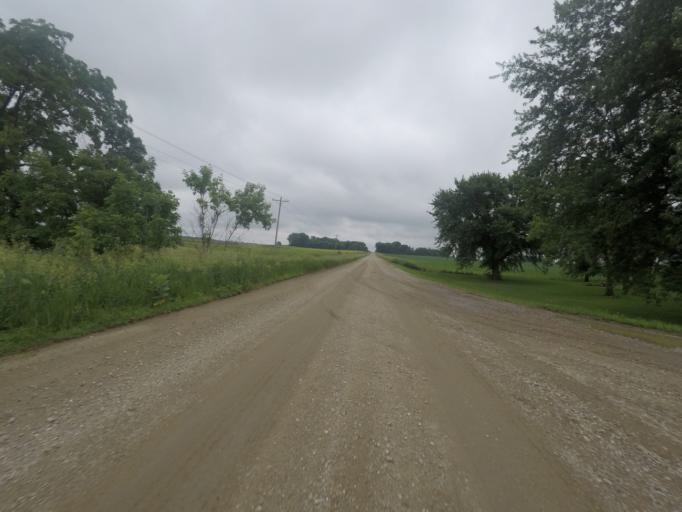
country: US
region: Minnesota
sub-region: Steele County
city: Owatonna
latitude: 44.0374
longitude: -93.0964
